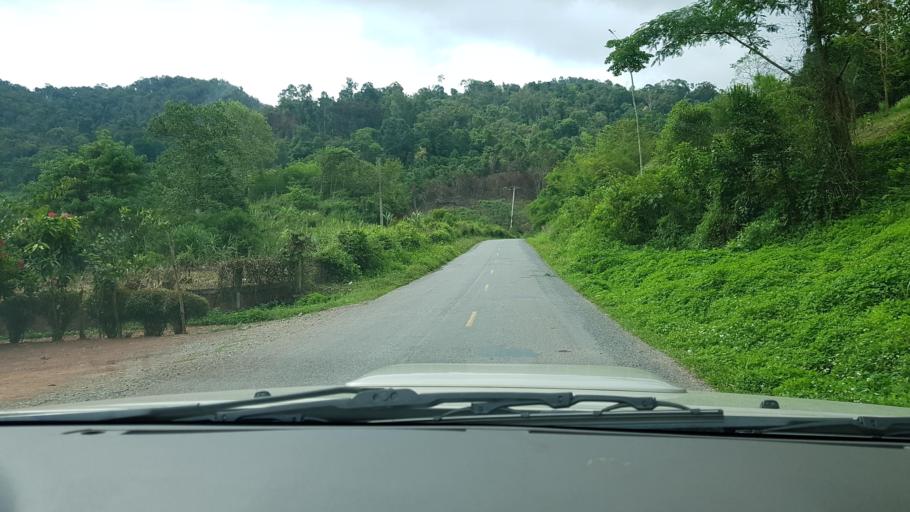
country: LA
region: Oudomxai
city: Muang Xay
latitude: 20.5688
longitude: 101.9199
